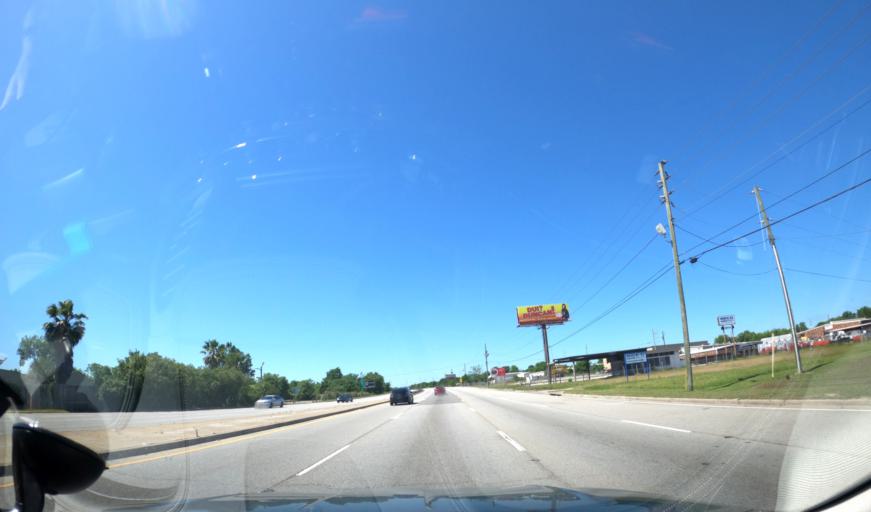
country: US
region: Georgia
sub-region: Richmond County
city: Augusta
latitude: 33.4546
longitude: -81.9701
